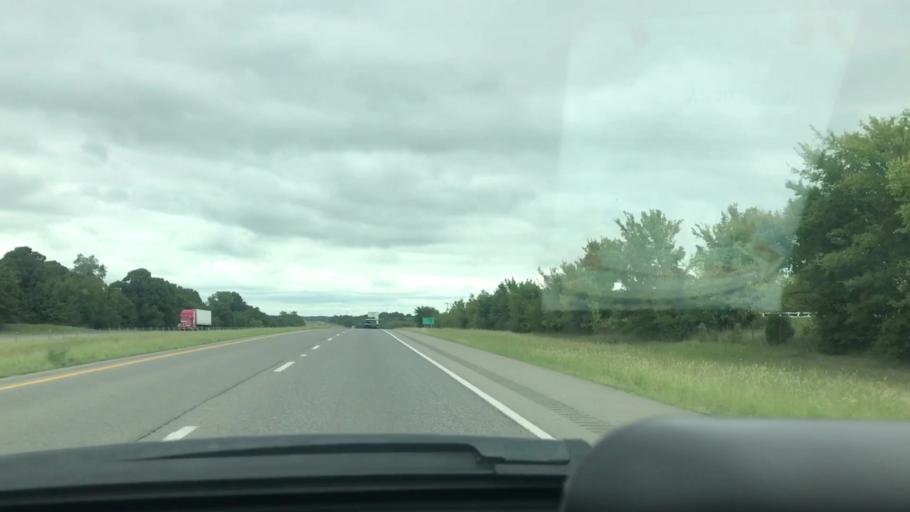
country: US
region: Oklahoma
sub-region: McIntosh County
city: Eufaula
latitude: 35.3723
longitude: -95.5708
